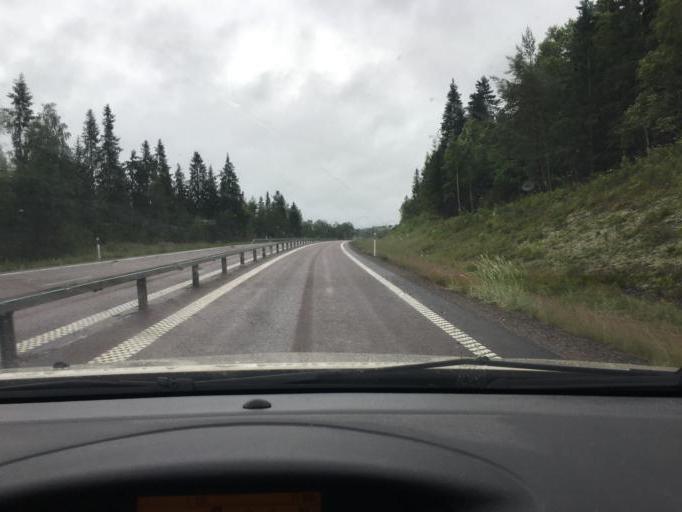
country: SE
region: Norrbotten
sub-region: Kalix Kommun
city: Rolfs
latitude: 65.8620
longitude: 23.0892
